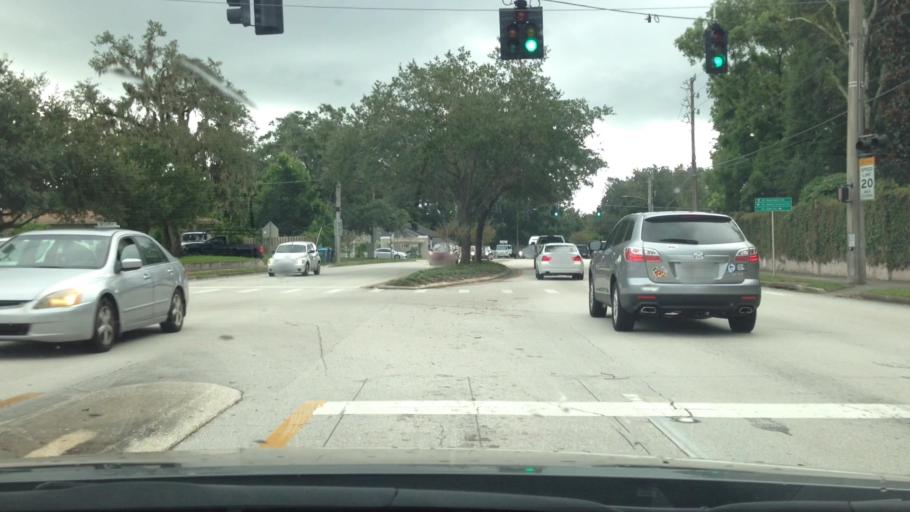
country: US
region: Florida
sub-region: Orange County
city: Maitland
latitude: 28.6280
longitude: -81.3467
